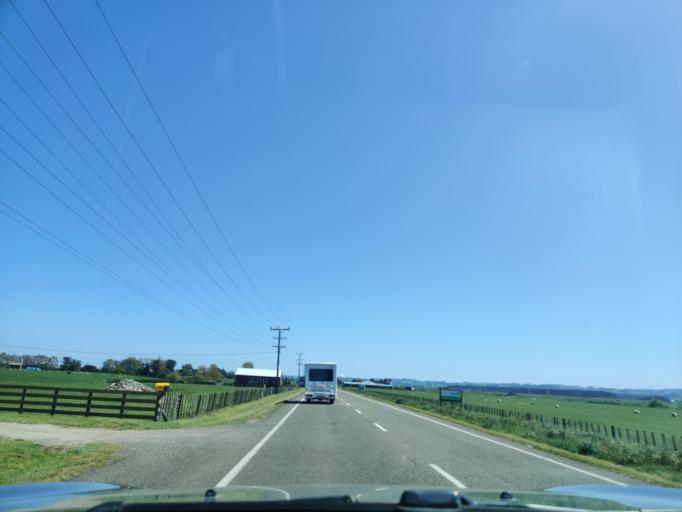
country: NZ
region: Manawatu-Wanganui
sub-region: Wanganui District
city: Wanganui
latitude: -39.8680
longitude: 174.9841
